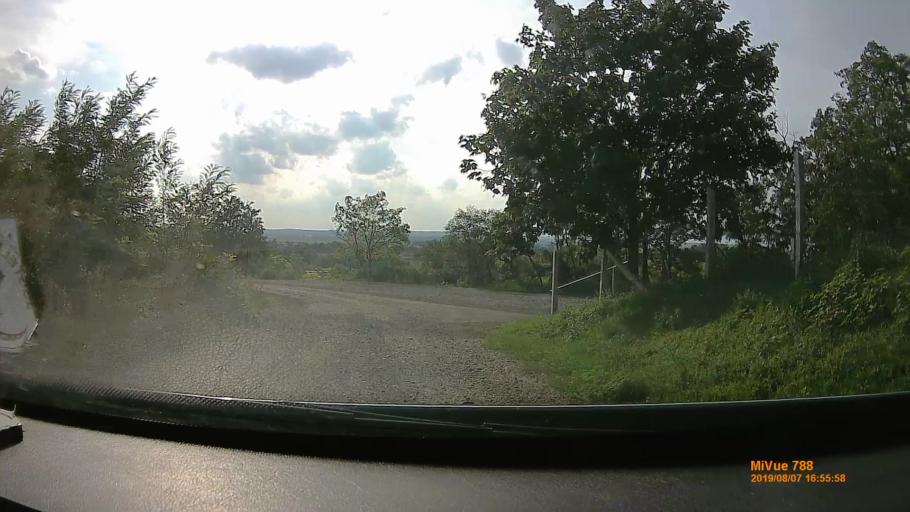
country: HU
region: Borsod-Abauj-Zemplen
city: Encs
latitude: 48.3173
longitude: 21.1670
